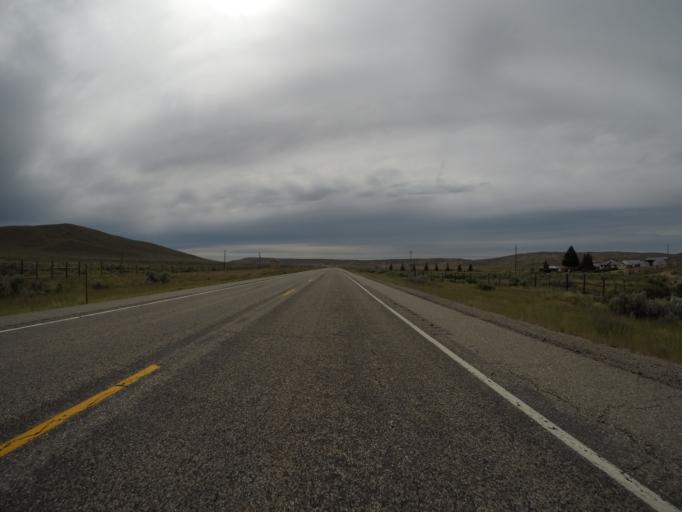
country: US
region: Utah
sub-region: Rich County
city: Randolph
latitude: 41.8243
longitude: -110.9057
